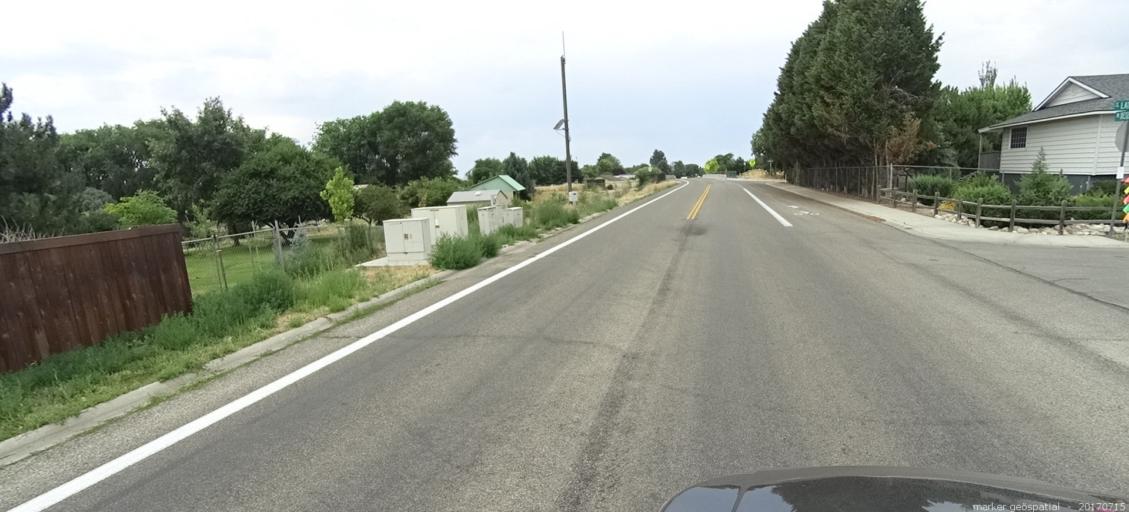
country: US
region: Idaho
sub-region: Ada County
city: Garden City
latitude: 43.5539
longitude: -116.2882
